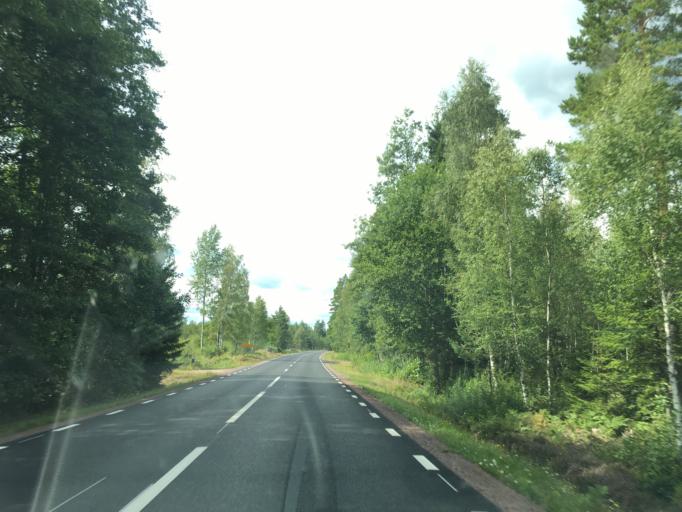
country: SE
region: Kalmar
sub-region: Nybro Kommun
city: Nybro
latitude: 56.9139
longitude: 16.0105
